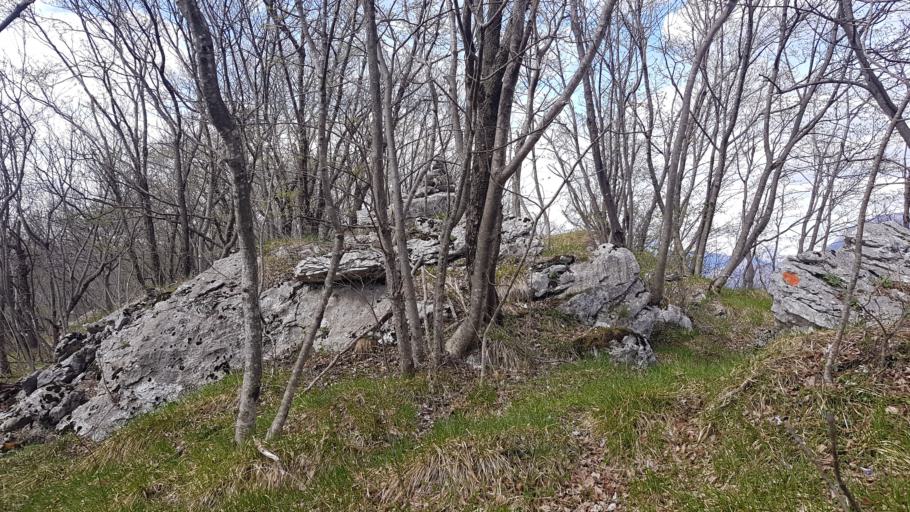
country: IT
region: Friuli Venezia Giulia
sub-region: Provincia di Udine
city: Trasaghis
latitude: 46.2798
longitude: 13.0469
